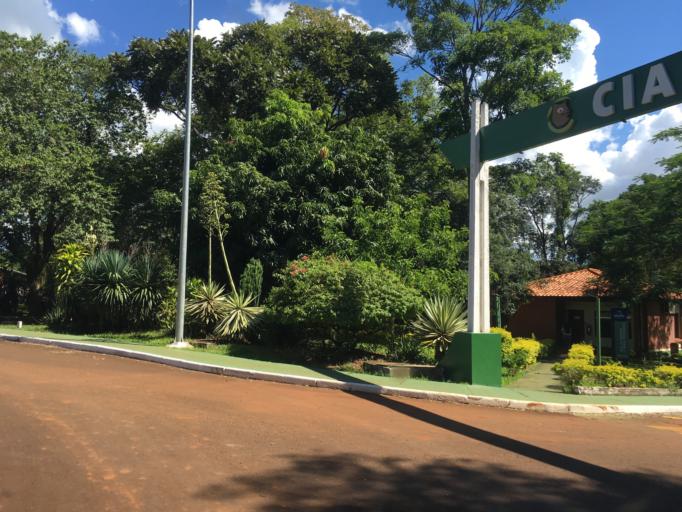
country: PY
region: Alto Parana
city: Ciudad del Este
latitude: -25.4466
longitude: -54.6339
